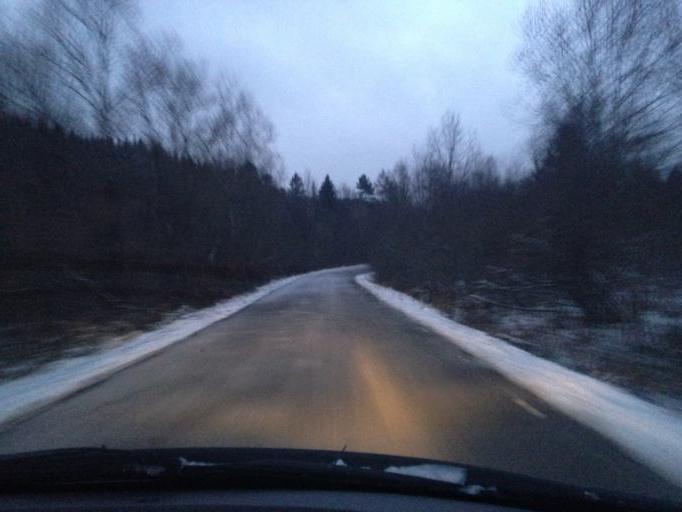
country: PL
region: Subcarpathian Voivodeship
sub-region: Powiat jasielski
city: Krempna
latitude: 49.5182
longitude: 21.5428
